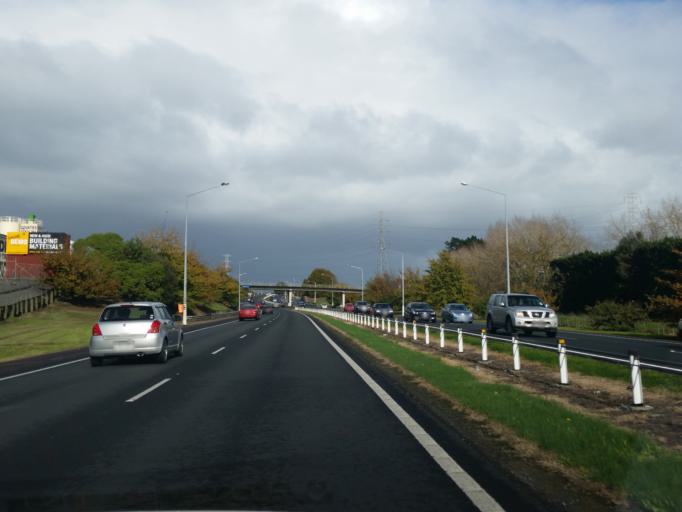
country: NZ
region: Auckland
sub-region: Auckland
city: Papakura
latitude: -37.1016
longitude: 174.9452
